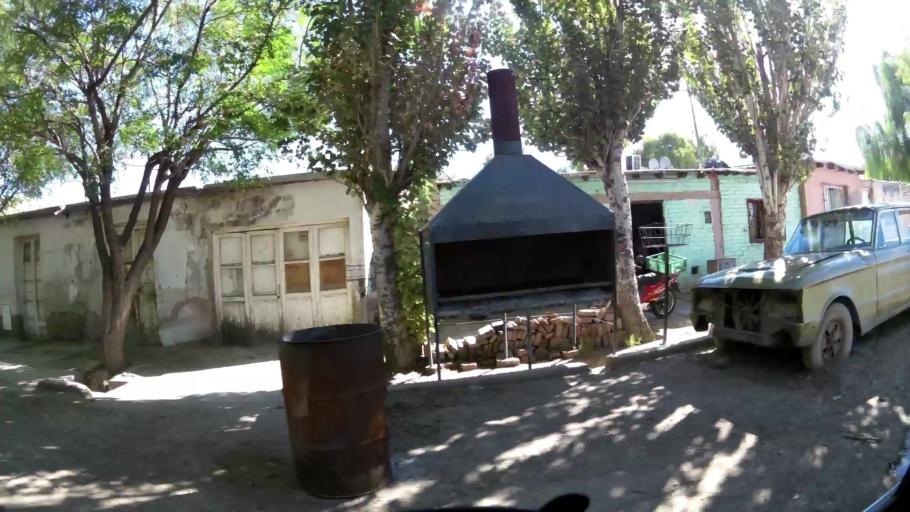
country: AR
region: Mendoza
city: Las Heras
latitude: -32.8392
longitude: -68.8043
